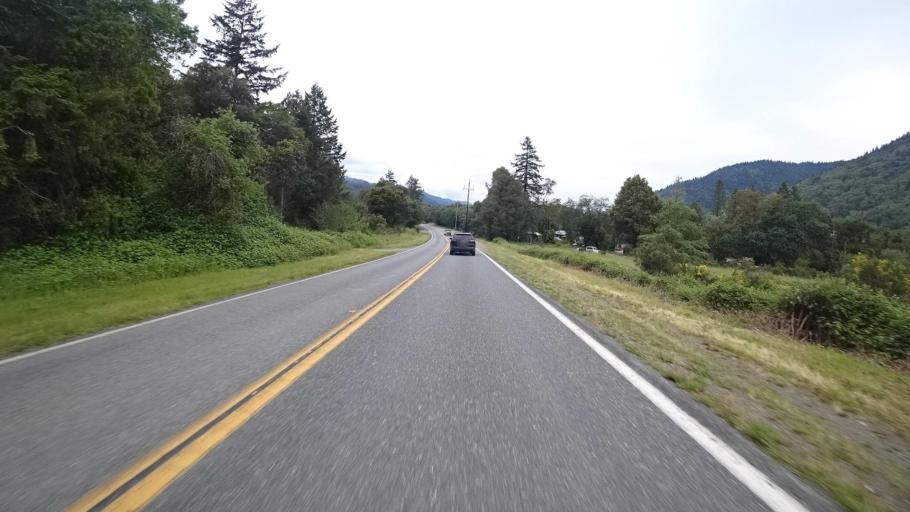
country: US
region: California
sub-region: Humboldt County
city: Willow Creek
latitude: 41.0236
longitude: -123.6513
